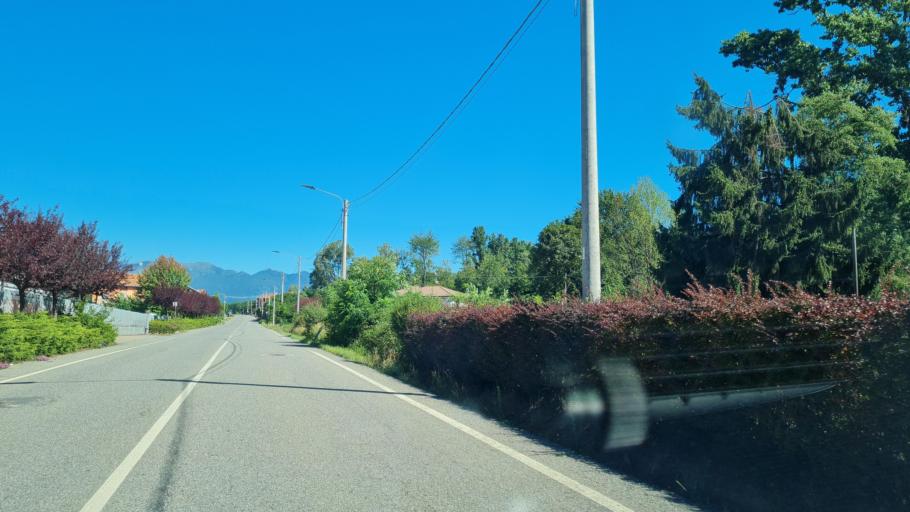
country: IT
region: Piedmont
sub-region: Provincia di Biella
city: Cossato
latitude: 45.5574
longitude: 8.2029
